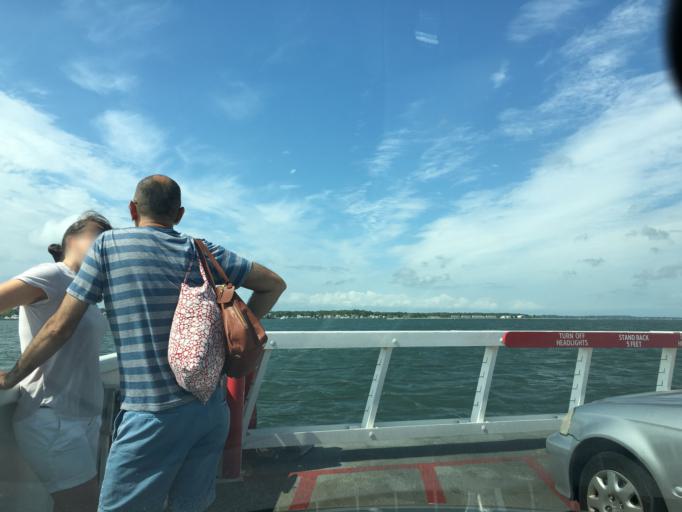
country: US
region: New York
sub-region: Suffolk County
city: Greenport
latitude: 41.0938
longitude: -72.3579
